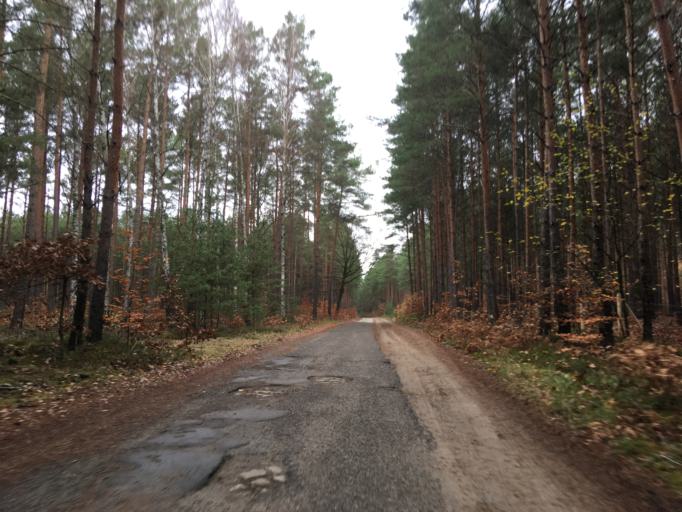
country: DE
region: Brandenburg
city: Jamlitz
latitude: 52.0638
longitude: 14.4826
